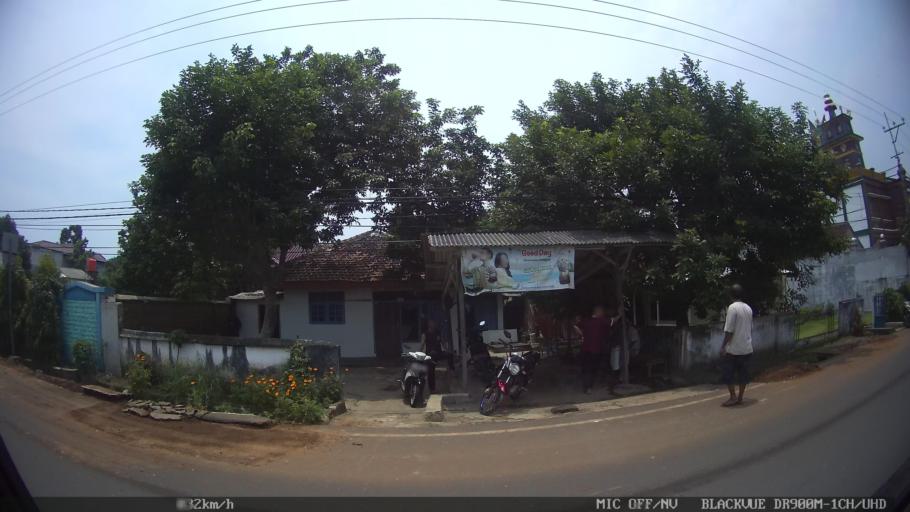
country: ID
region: Lampung
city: Bandarlampung
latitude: -5.4120
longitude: 105.2726
